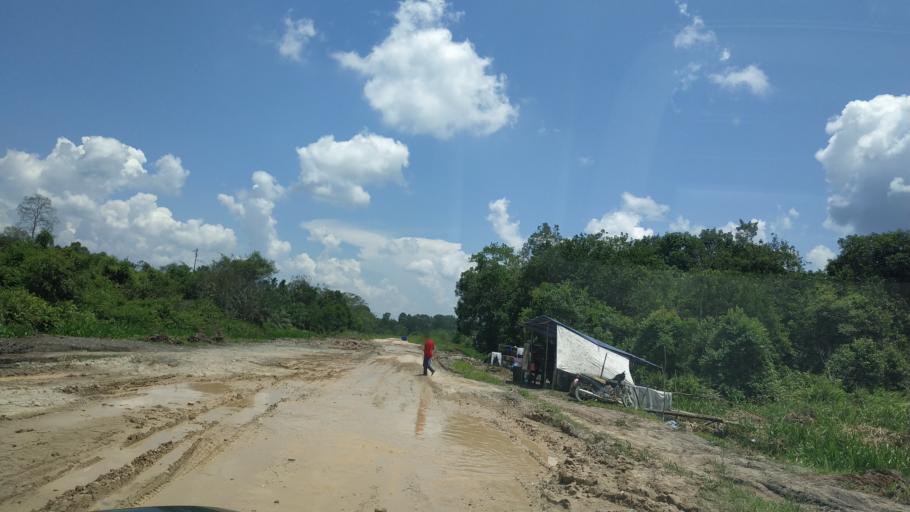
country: ID
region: Riau
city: Pangkalanbunut
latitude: 0.1937
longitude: 102.3826
